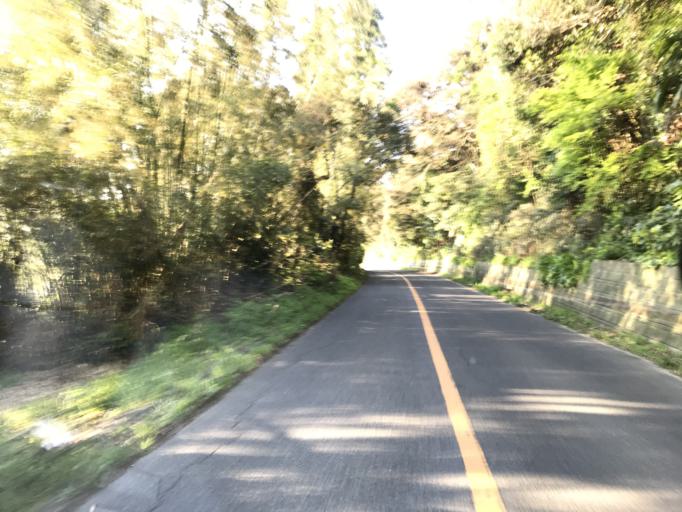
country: JP
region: Chiba
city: Yokaichiba
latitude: 35.7197
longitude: 140.5635
